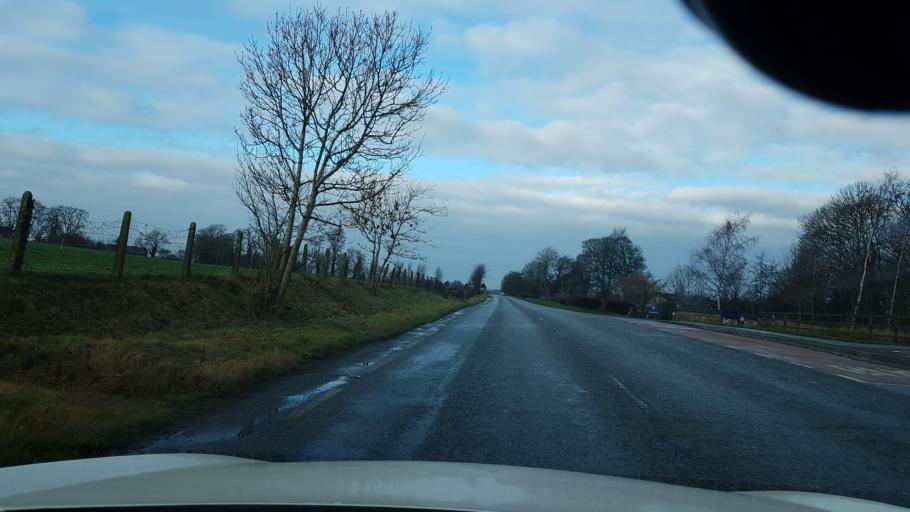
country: IE
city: Kentstown
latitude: 53.5891
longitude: -6.5963
